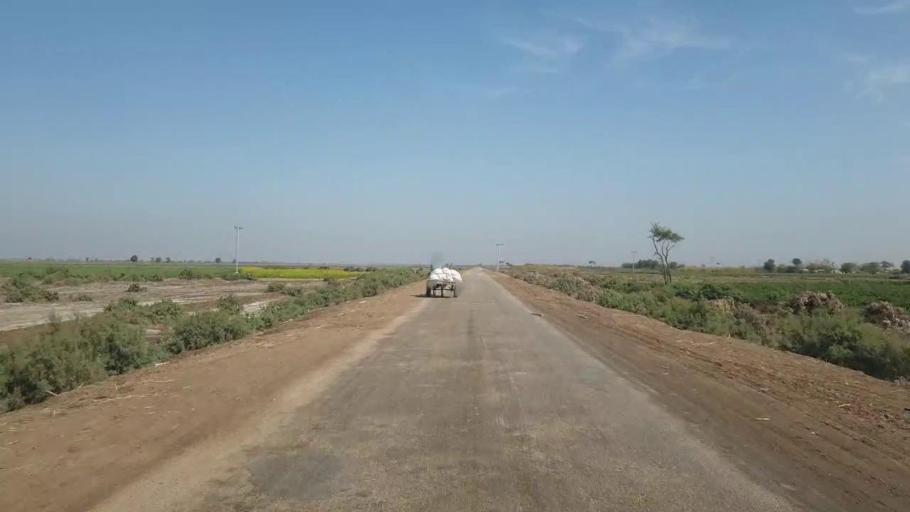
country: PK
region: Sindh
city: Samaro
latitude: 25.3453
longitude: 69.2491
